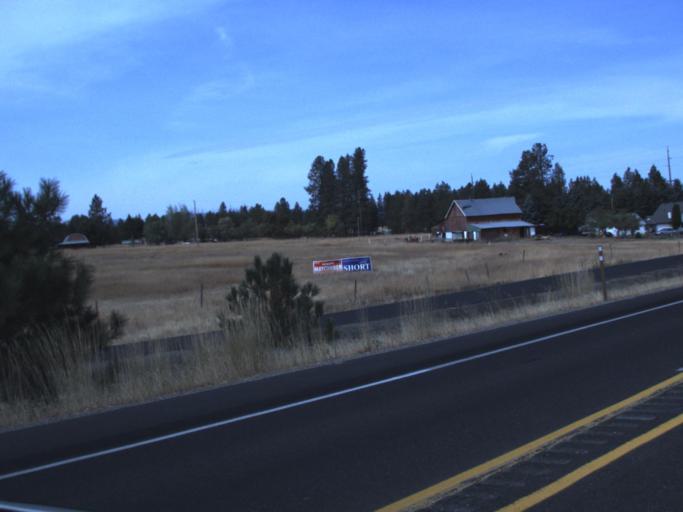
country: US
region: Washington
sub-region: Spokane County
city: Deer Park
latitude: 47.9313
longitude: -117.4664
